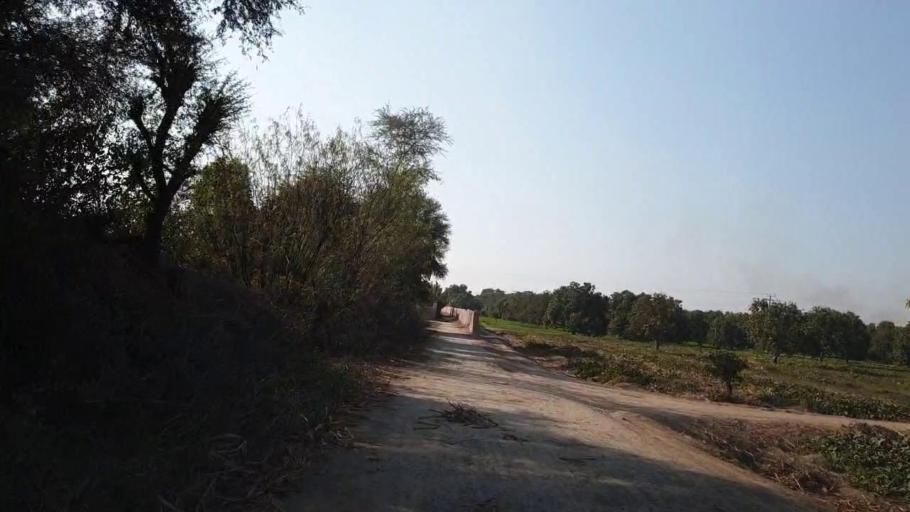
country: PK
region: Sindh
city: Tando Jam
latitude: 25.4871
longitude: 68.5360
